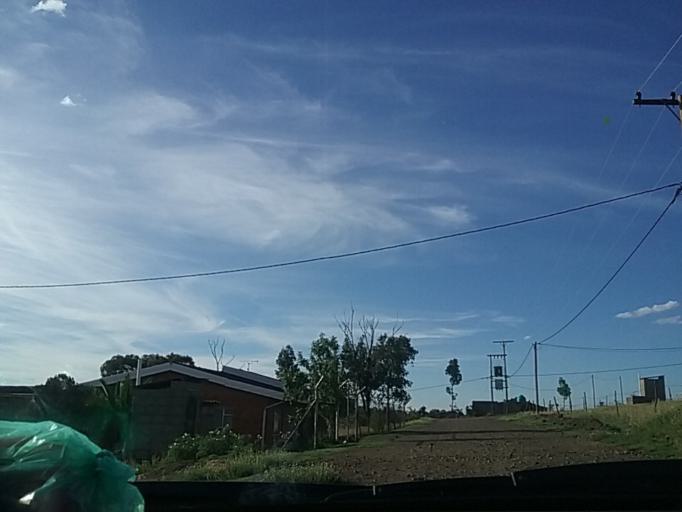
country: LS
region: Berea
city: Teyateyaneng
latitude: -29.1493
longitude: 27.7381
